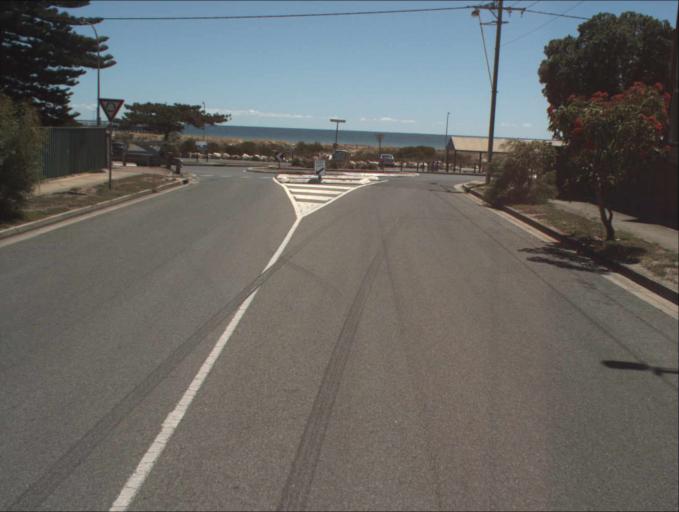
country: AU
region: South Australia
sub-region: Port Adelaide Enfield
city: Birkenhead
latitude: -34.8246
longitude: 138.4874
